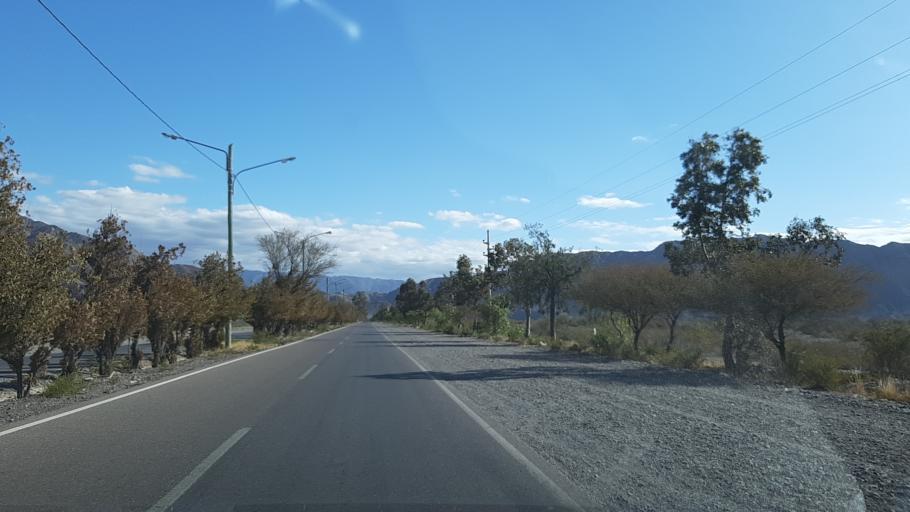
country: AR
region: San Juan
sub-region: Departamento de Rivadavia
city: Rivadavia
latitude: -31.5450
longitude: -68.6495
